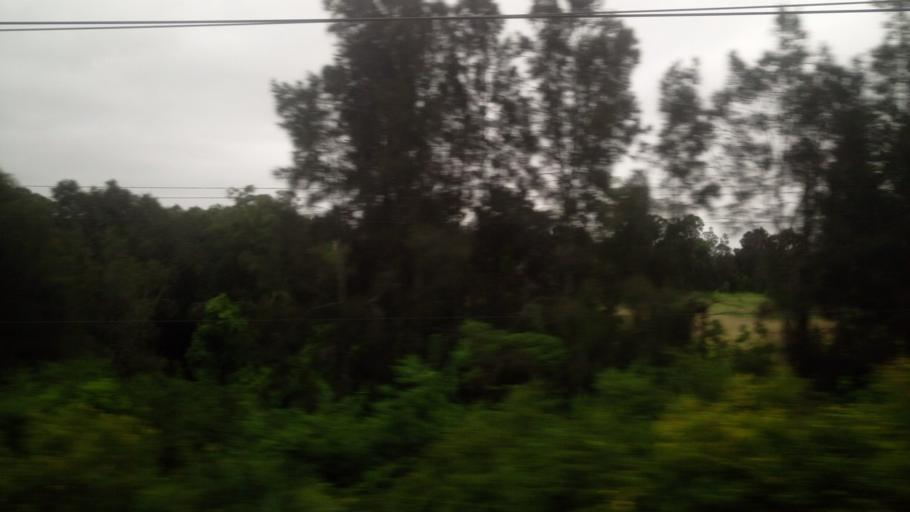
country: AU
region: New South Wales
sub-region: Blacktown
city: Mount Druitt
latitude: -33.7657
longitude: 150.7974
